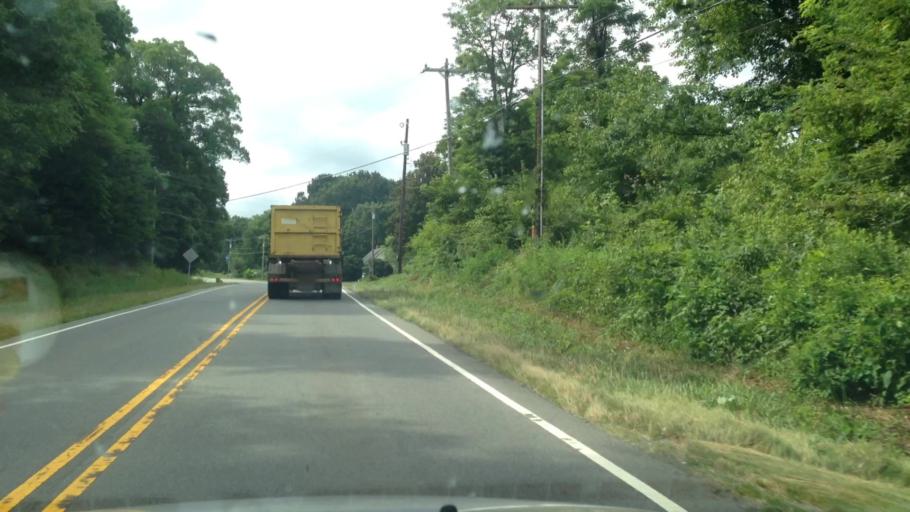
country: US
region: North Carolina
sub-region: Rockingham County
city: Wentworth
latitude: 36.3966
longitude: -79.7582
